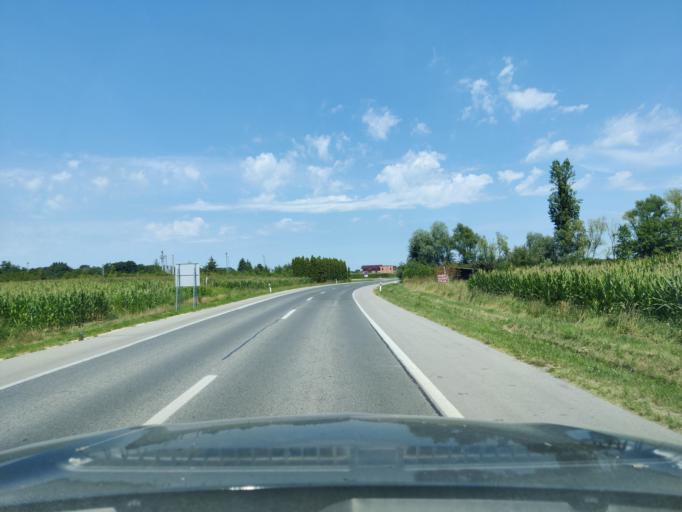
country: HR
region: Medimurska
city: Mackovec
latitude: 46.4343
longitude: 16.4308
